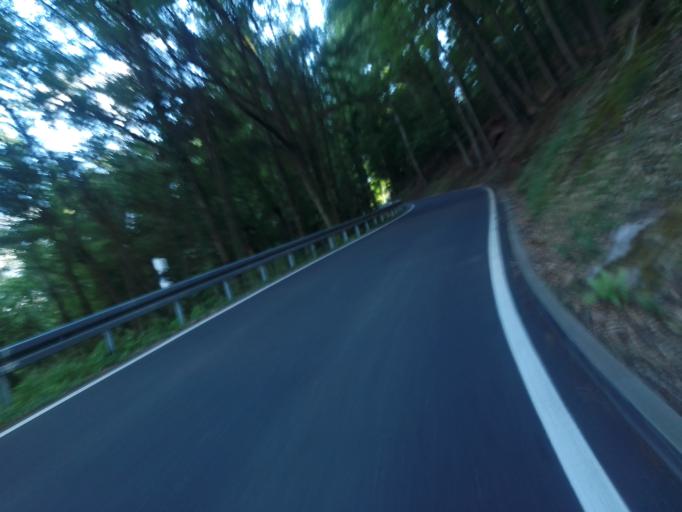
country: DE
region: Bavaria
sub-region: Regierungsbezirk Unterfranken
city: Hasloch
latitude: 49.7949
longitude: 9.4909
